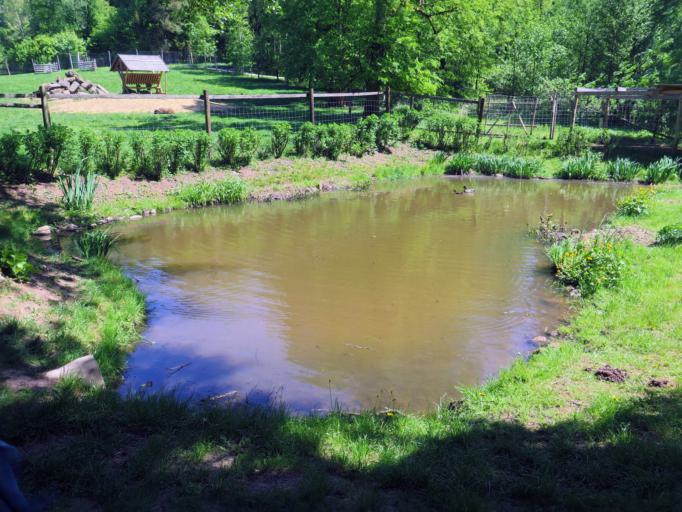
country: DE
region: Bavaria
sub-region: Upper Franconia
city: Weitramsdorf
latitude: 50.2292
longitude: 10.8635
